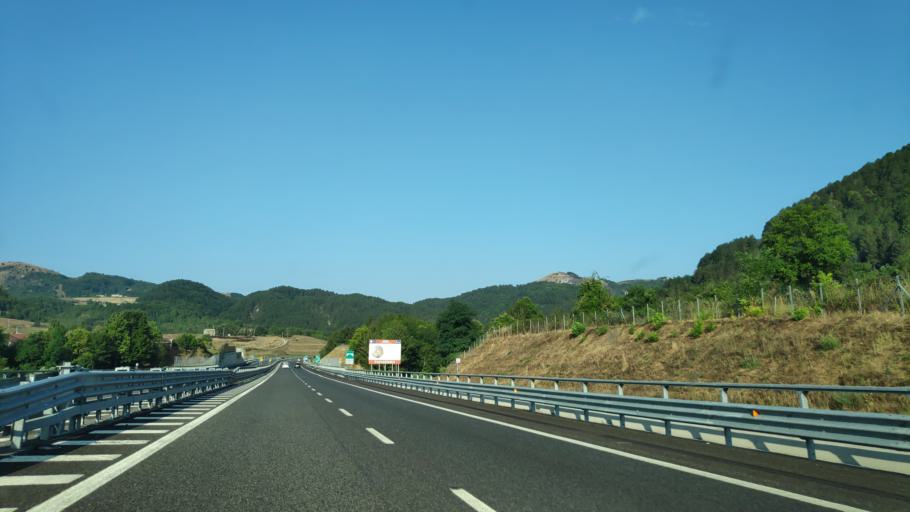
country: IT
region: Calabria
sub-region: Provincia di Cosenza
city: Mormanno
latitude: 39.8780
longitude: 16.0008
